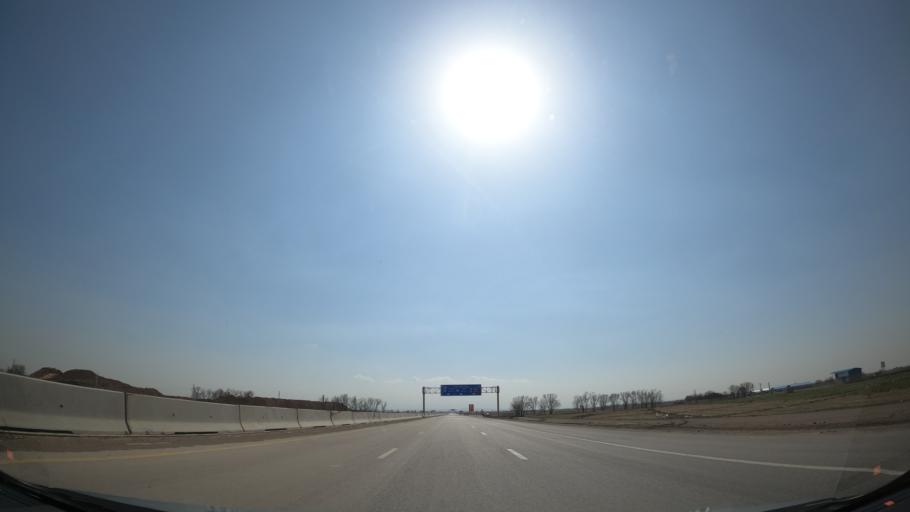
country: IR
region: Qazvin
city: Abyek
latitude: 35.9805
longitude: 50.4613
